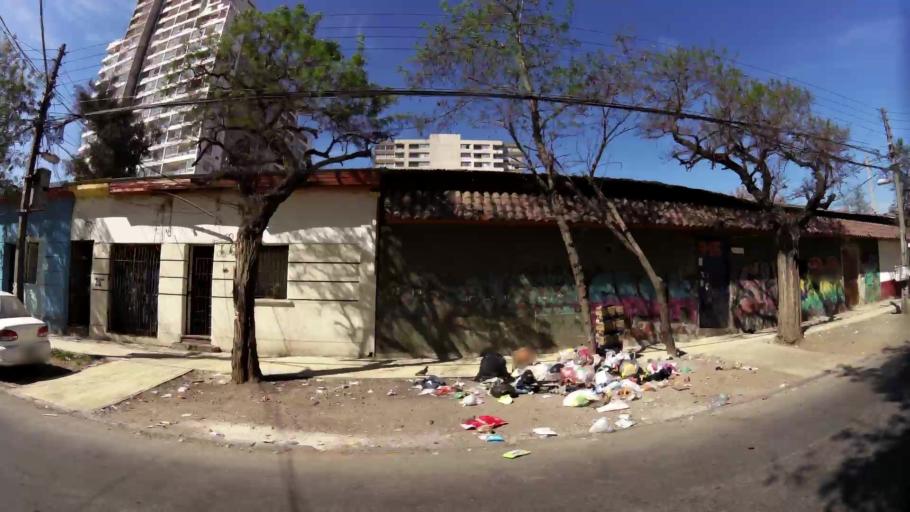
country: CL
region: Santiago Metropolitan
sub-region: Provincia de Santiago
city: Santiago
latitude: -33.4210
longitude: -70.6604
